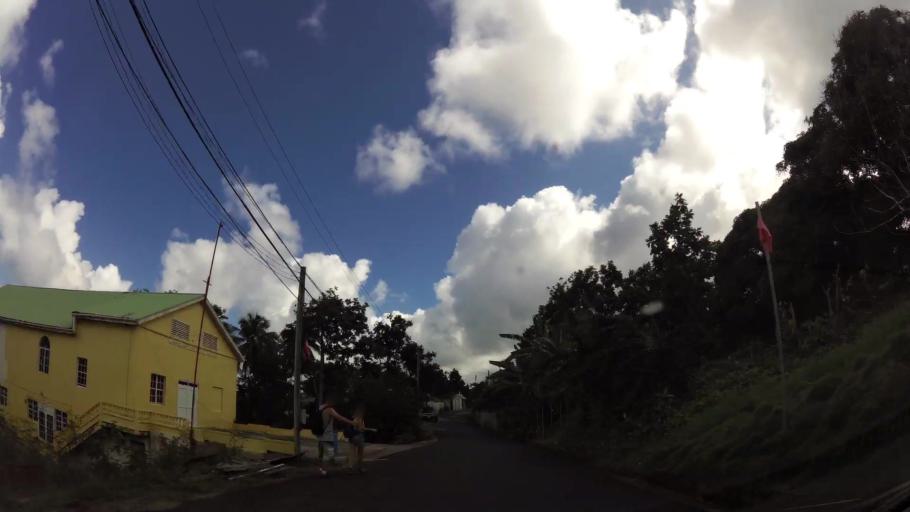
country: DM
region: Saint Andrew
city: Calibishie
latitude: 15.6148
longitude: -61.4043
